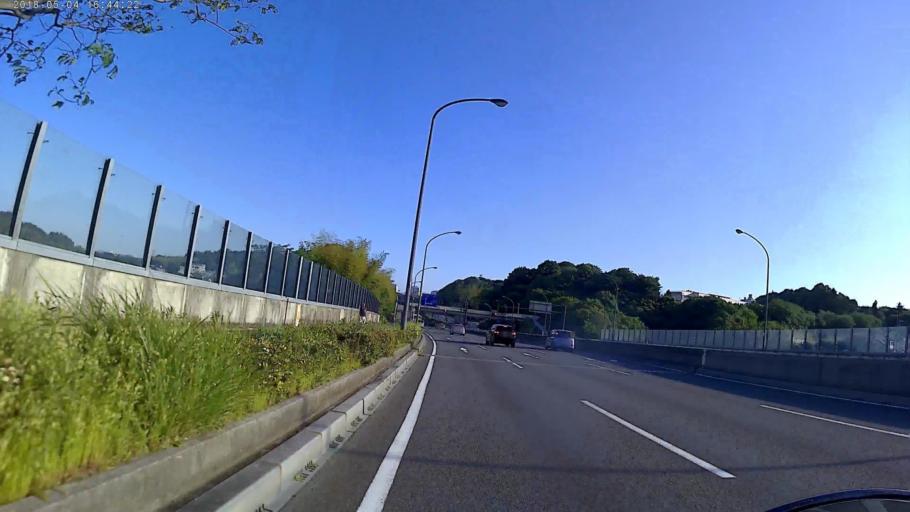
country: JP
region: Kanagawa
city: Yokohama
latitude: 35.4491
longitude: 139.5603
